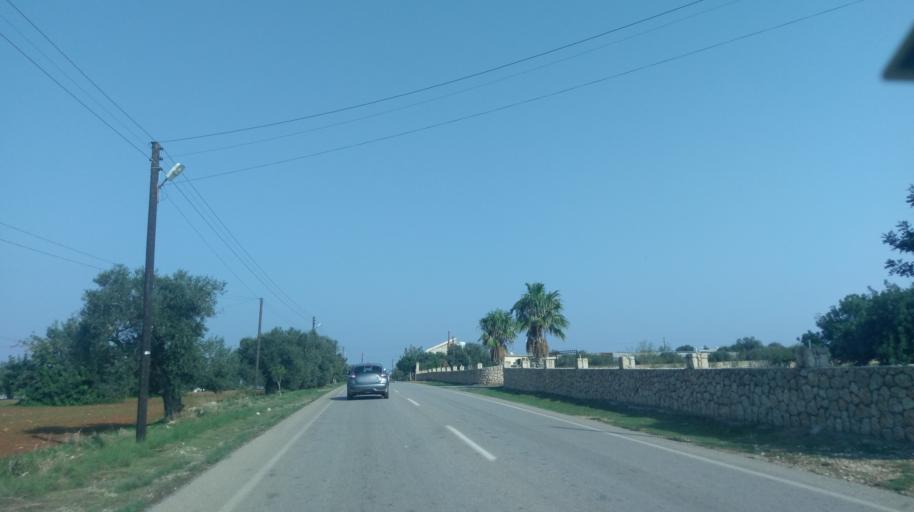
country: CY
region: Ammochostos
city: Leonarisso
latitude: 35.5232
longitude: 34.1758
